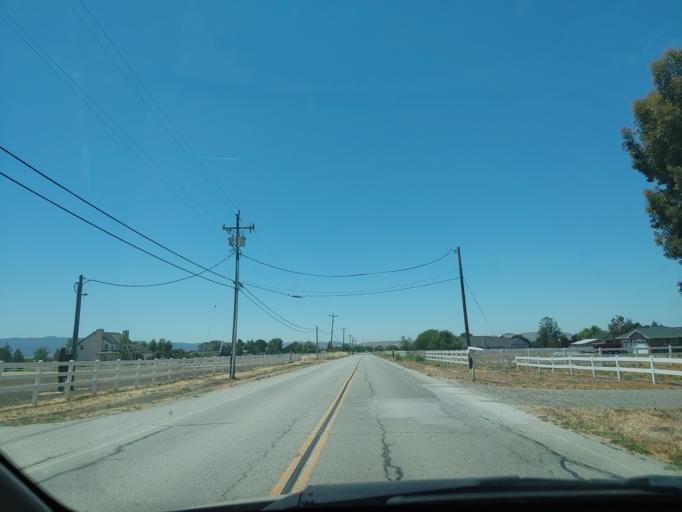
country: US
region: California
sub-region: San Benito County
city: Hollister
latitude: 36.9132
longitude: -121.3623
